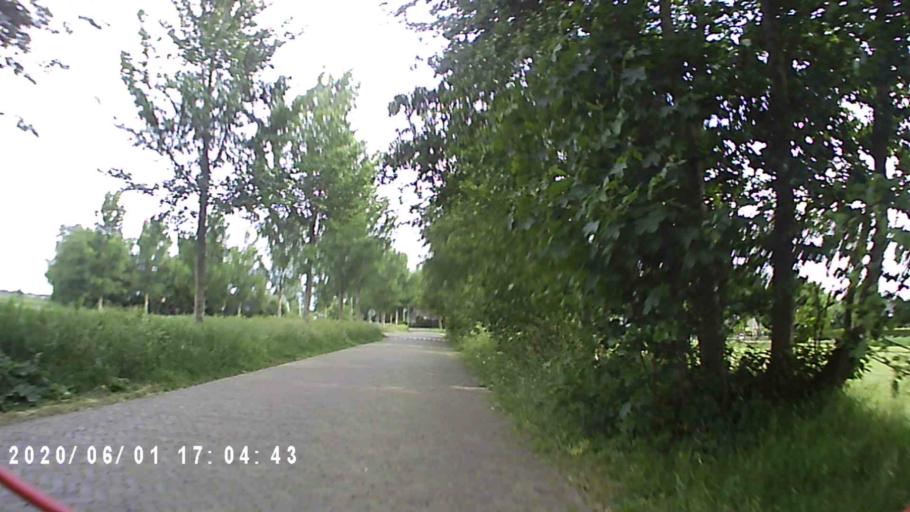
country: NL
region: Friesland
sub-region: Gemeente Tytsjerksteradiel
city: Garyp
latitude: 53.1734
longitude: 5.9337
